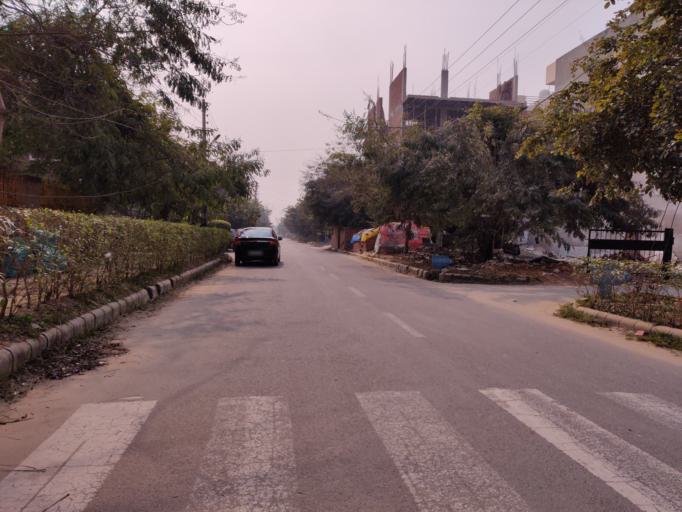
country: IN
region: Haryana
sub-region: Gurgaon
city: Gurgaon
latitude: 28.4421
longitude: 77.0692
